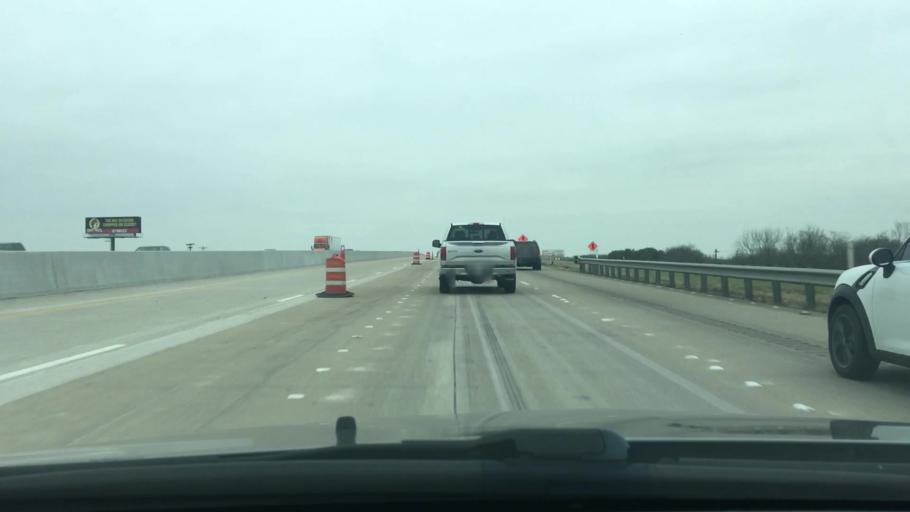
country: US
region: Texas
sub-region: Navarro County
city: Corsicana
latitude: 32.0975
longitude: -96.4411
